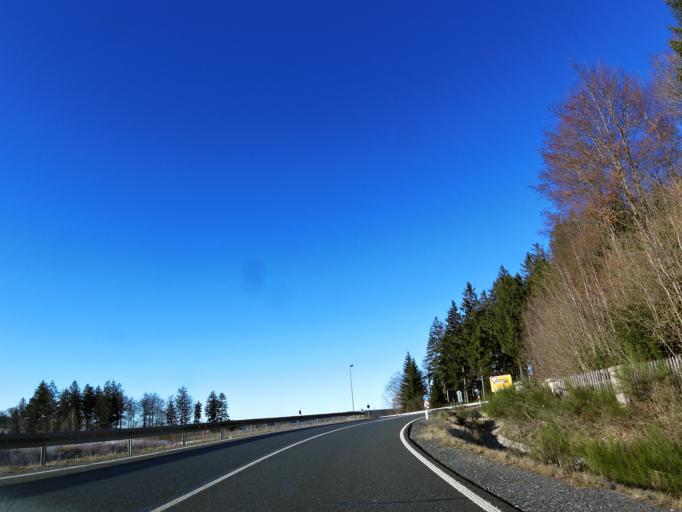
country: DE
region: Bavaria
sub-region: Upper Franconia
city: Bischofsgrun
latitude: 50.0548
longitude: 11.8213
